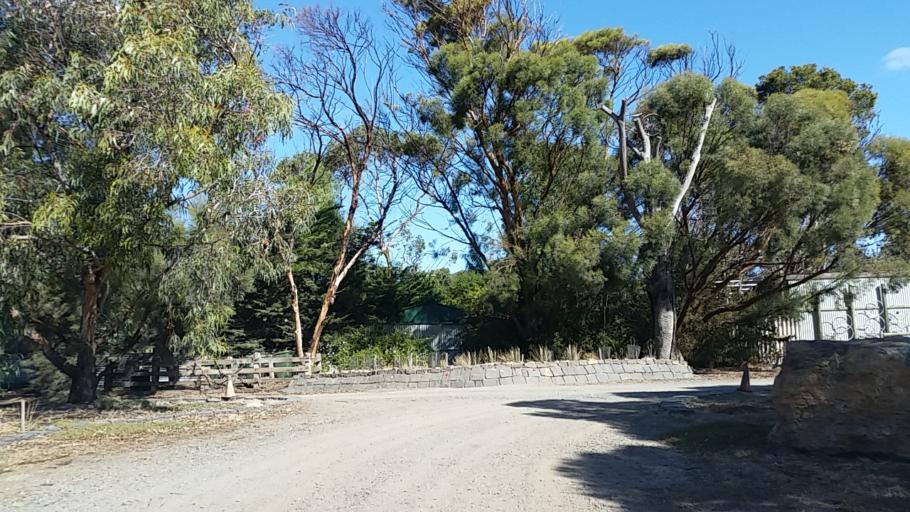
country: AU
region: South Australia
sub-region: Onkaparinga
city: Aldinga
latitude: -35.2667
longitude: 138.4801
